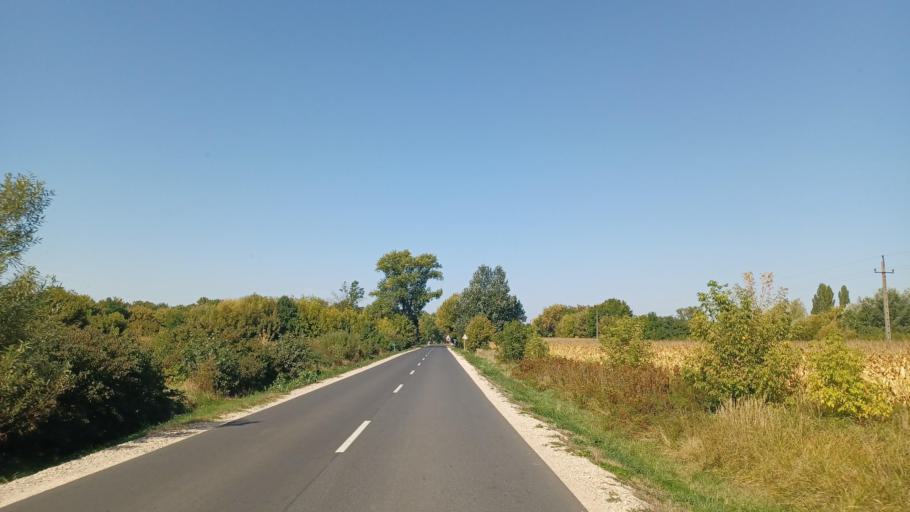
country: HU
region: Fejer
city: Cece
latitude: 46.7627
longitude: 18.6457
